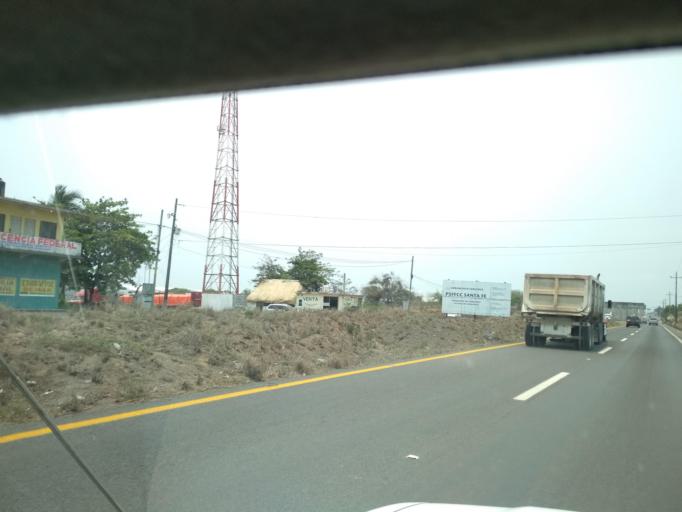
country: MX
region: Veracruz
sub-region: Veracruz
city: Delfino Victoria (Santa Fe)
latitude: 19.2054
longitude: -96.2657
